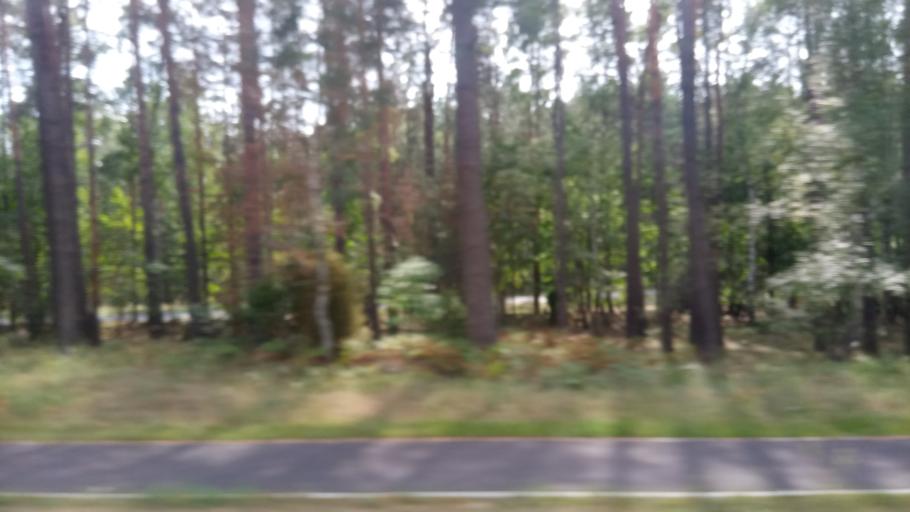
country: PL
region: Greater Poland Voivodeship
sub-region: Powiat pilski
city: Kaczory
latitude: 53.1154
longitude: 16.8357
